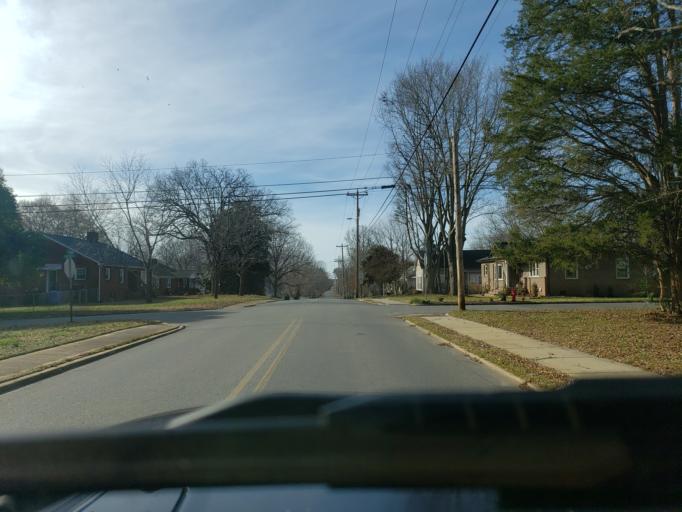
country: US
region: North Carolina
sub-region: Cleveland County
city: Kings Mountain
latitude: 35.2381
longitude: -81.3527
